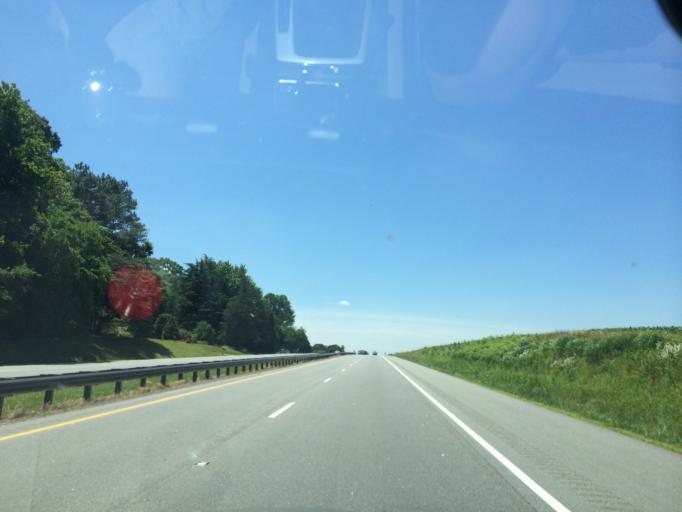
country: US
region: Maryland
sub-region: Talbot County
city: Easton
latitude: 38.7509
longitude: -76.0652
